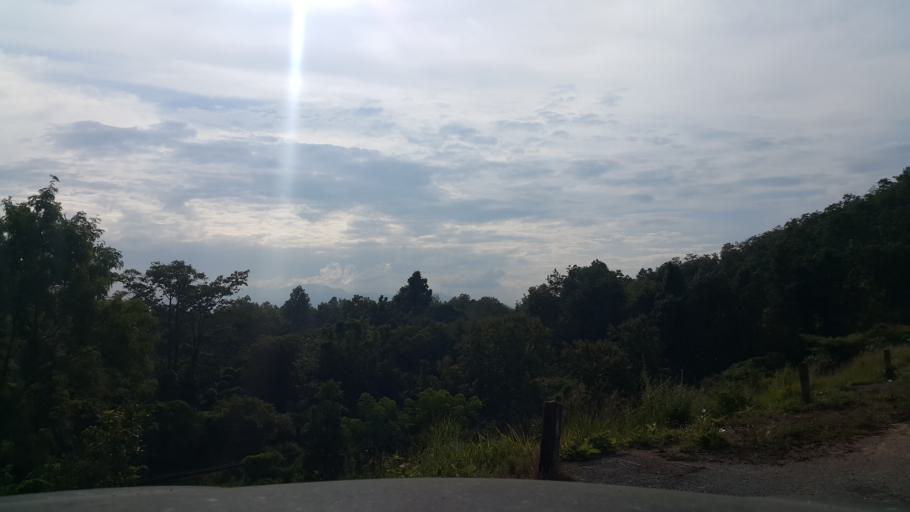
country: TH
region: Chiang Mai
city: San Sai
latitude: 18.9221
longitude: 99.0915
